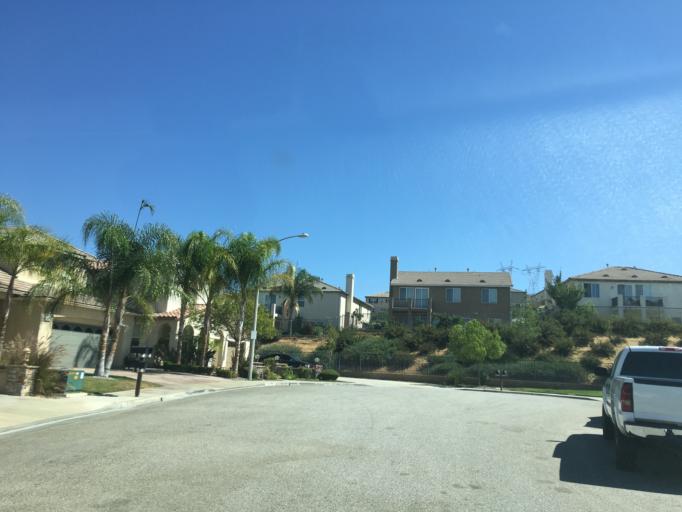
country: US
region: California
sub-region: Los Angeles County
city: Santa Clarita
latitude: 34.4494
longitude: -118.4812
